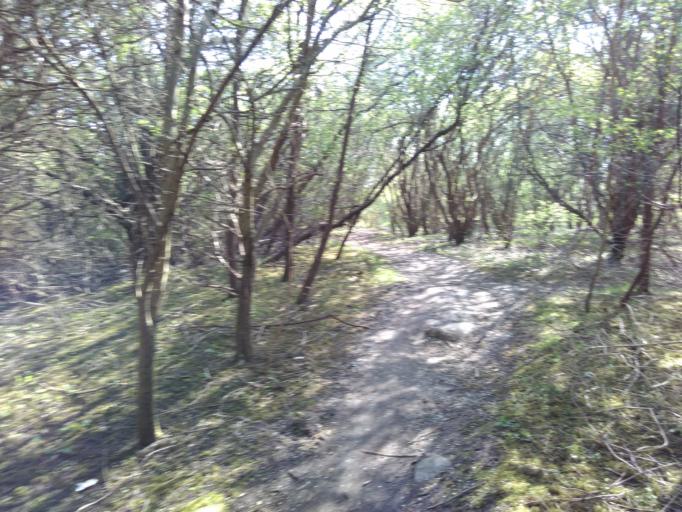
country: DK
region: Capital Region
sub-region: Kobenhavn
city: Copenhagen
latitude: 55.6540
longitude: 12.5789
